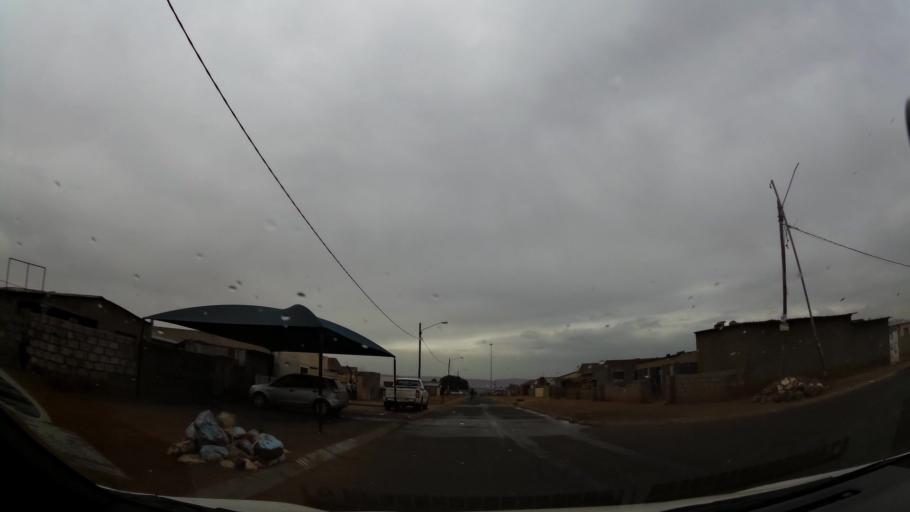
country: ZA
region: Gauteng
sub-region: Ekurhuleni Metropolitan Municipality
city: Germiston
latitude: -26.3856
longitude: 28.1771
